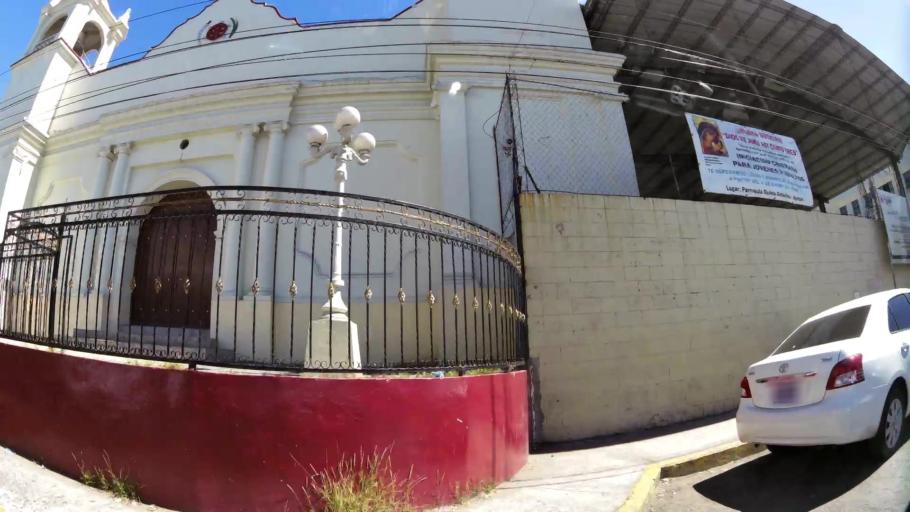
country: SV
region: San Salvador
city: Apopa
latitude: 13.8019
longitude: -89.1786
